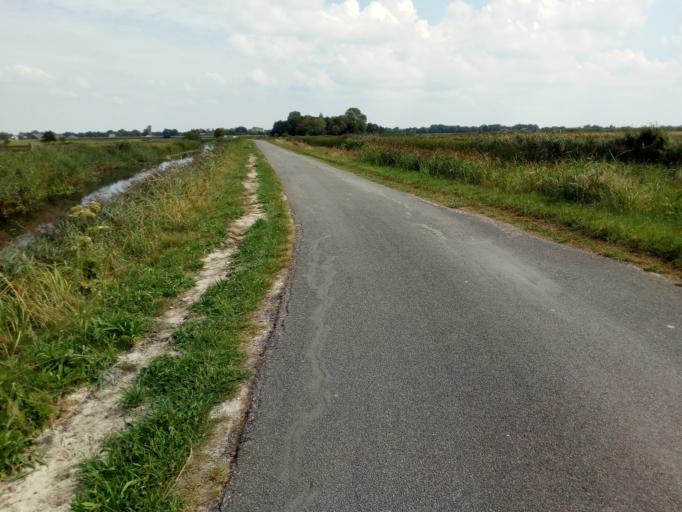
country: NL
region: Friesland
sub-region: Gemeente Smallingerland
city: Oudega
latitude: 53.1202
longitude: 5.9578
